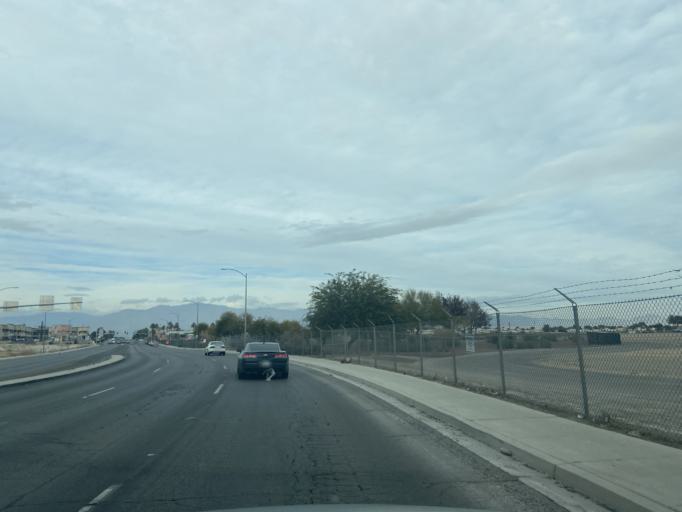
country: US
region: Nevada
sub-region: Clark County
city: Las Vegas
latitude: 36.2141
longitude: -115.2075
